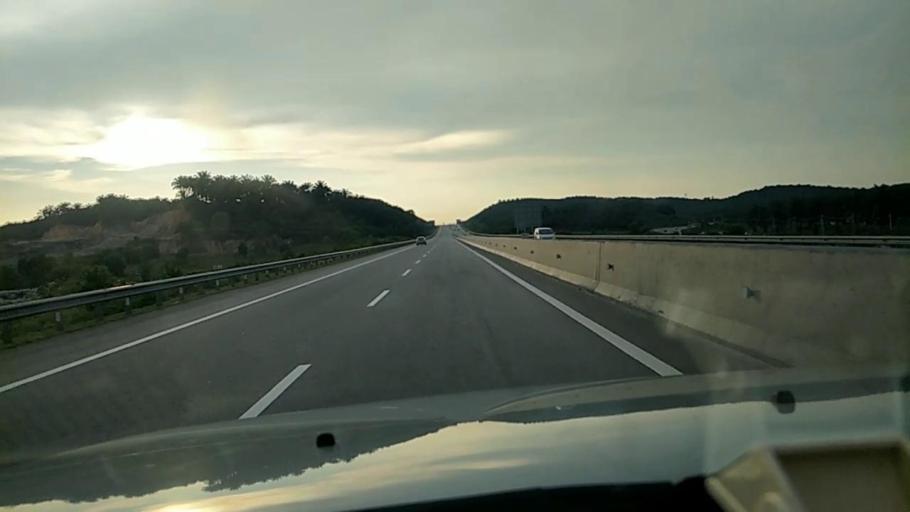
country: MY
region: Selangor
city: Batu Arang
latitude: 3.2777
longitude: 101.4519
